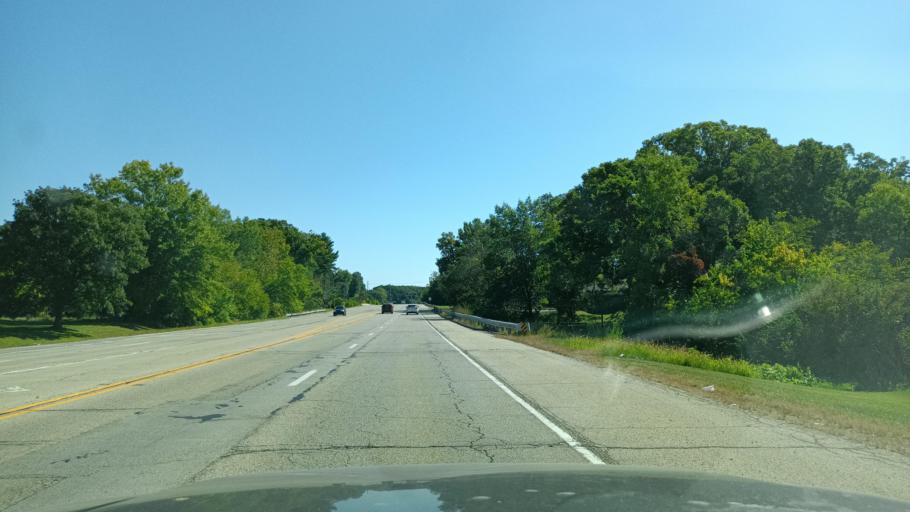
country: US
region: Illinois
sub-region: Peoria County
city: West Peoria
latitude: 40.7701
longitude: -89.6530
